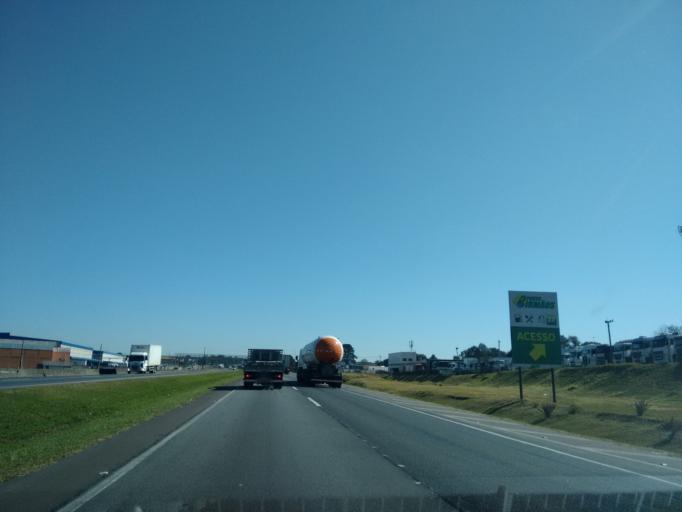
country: BR
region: Parana
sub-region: Sao Jose Dos Pinhais
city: Sao Jose dos Pinhais
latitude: -25.5518
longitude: -49.2791
